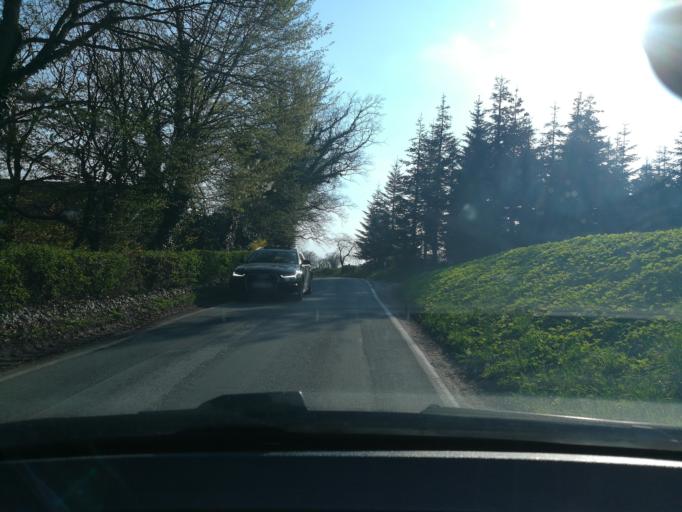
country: DE
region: North Rhine-Westphalia
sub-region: Regierungsbezirk Detmold
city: Werther
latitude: 52.0390
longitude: 8.4118
